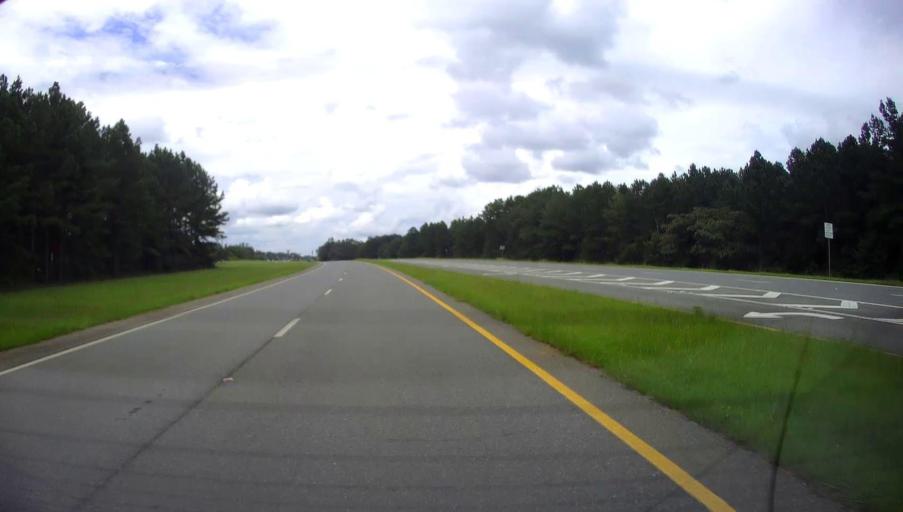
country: US
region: Georgia
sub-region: Schley County
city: Ellaville
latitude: 32.2326
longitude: -84.2937
